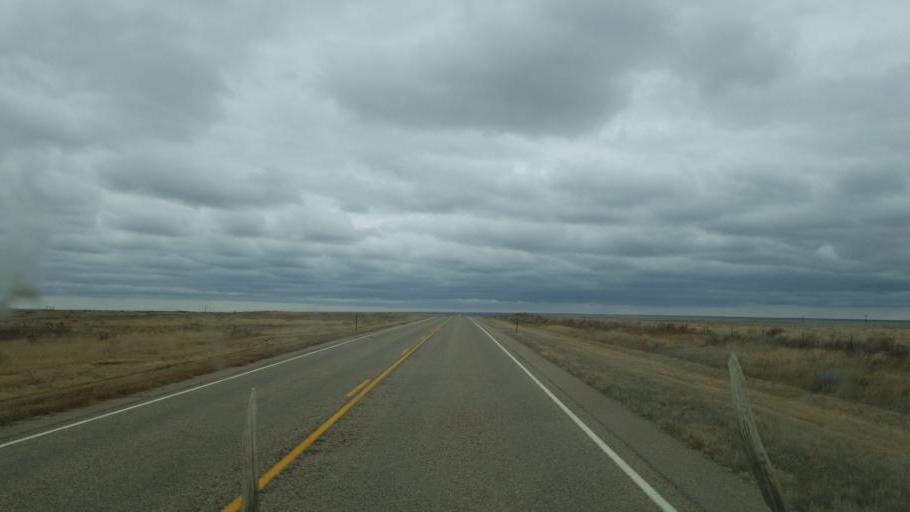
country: US
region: Colorado
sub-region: Kiowa County
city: Eads
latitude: 38.7761
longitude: -102.7396
